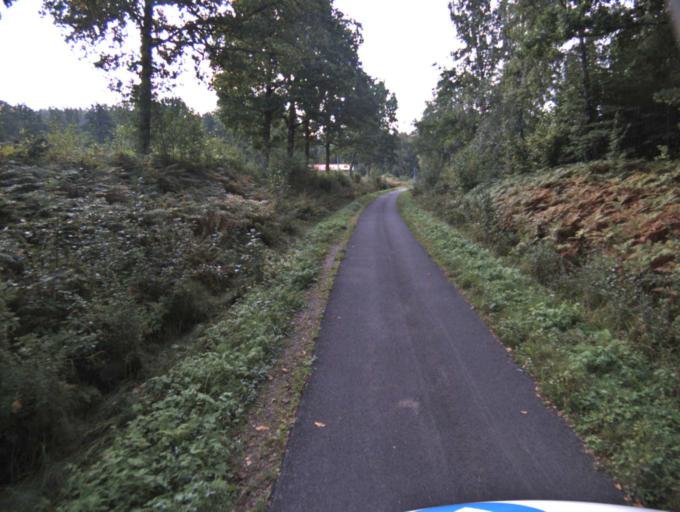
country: SE
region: Vaestra Goetaland
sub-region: Ulricehamns Kommun
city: Ulricehamn
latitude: 57.7097
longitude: 13.3974
